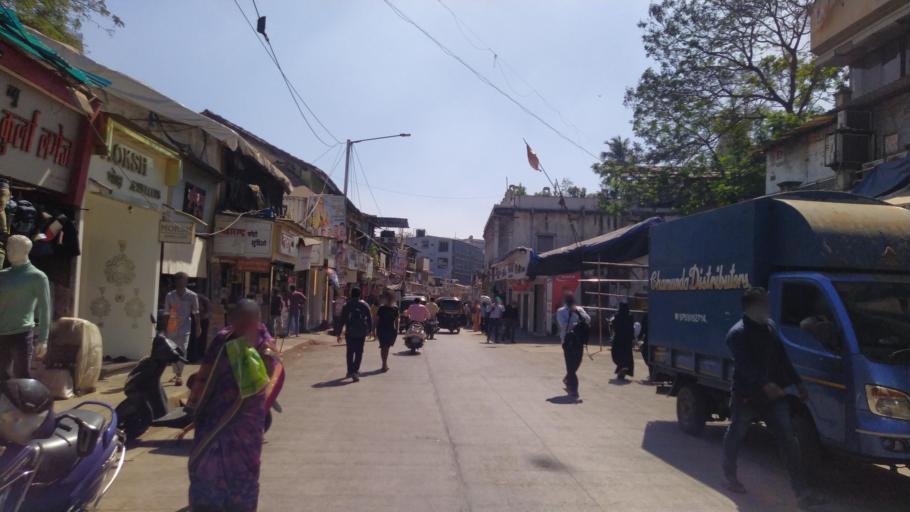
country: IN
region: Maharashtra
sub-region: Mumbai Suburban
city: Mumbai
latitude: 19.0684
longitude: 72.8779
